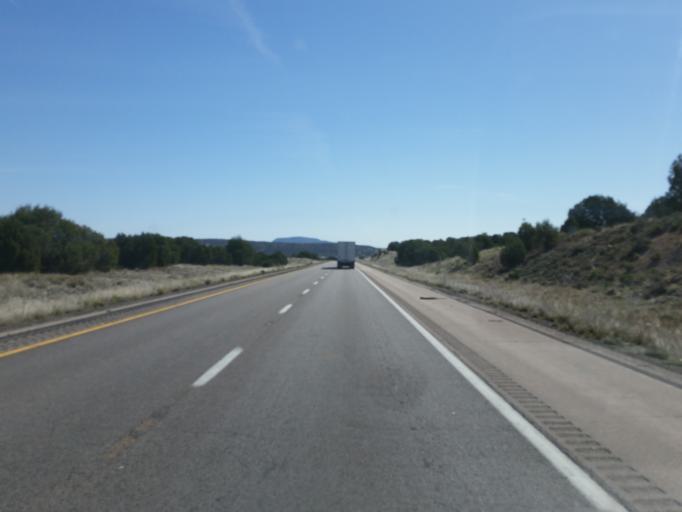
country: US
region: Arizona
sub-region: Mohave County
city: Peach Springs
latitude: 35.2220
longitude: -113.2430
